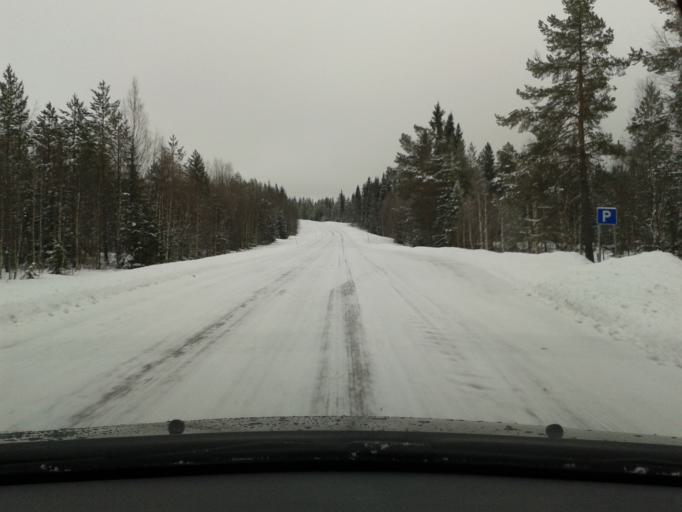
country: SE
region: Vaesterbotten
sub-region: Vilhelmina Kommun
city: Sjoberg
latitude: 64.8627
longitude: 15.8961
